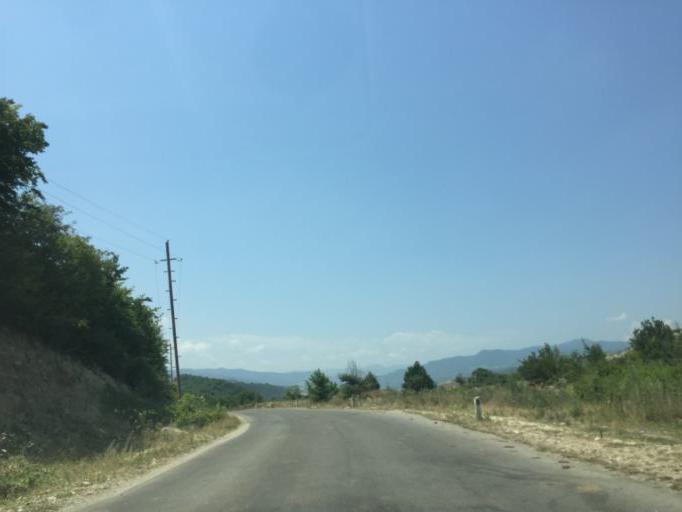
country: AZ
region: Tartar Rayon
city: Martakert
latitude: 40.1425
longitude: 46.5582
